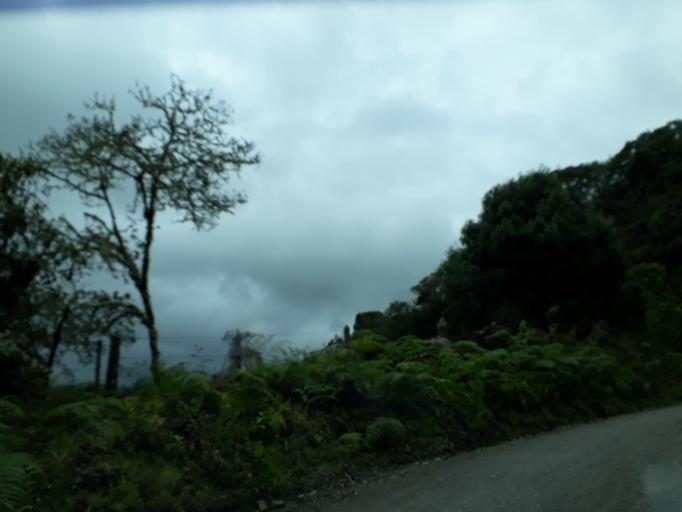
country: CO
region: Cundinamarca
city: Junin
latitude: 4.6840
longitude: -73.6766
